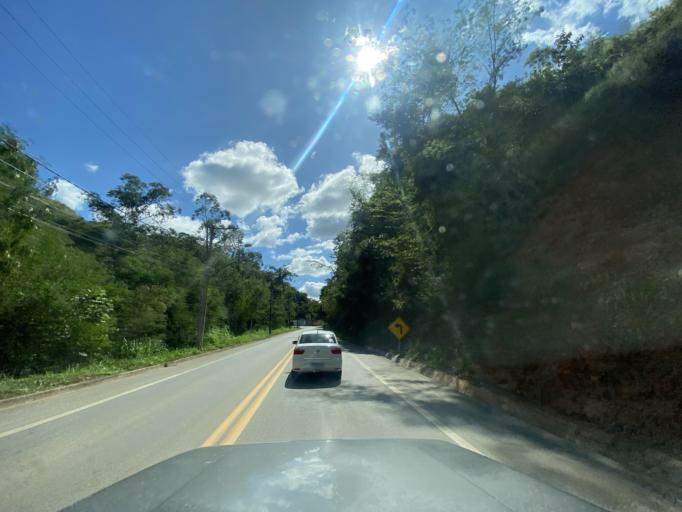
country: BR
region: Espirito Santo
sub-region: Alegre
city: Alegre
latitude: -20.7611
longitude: -41.5220
